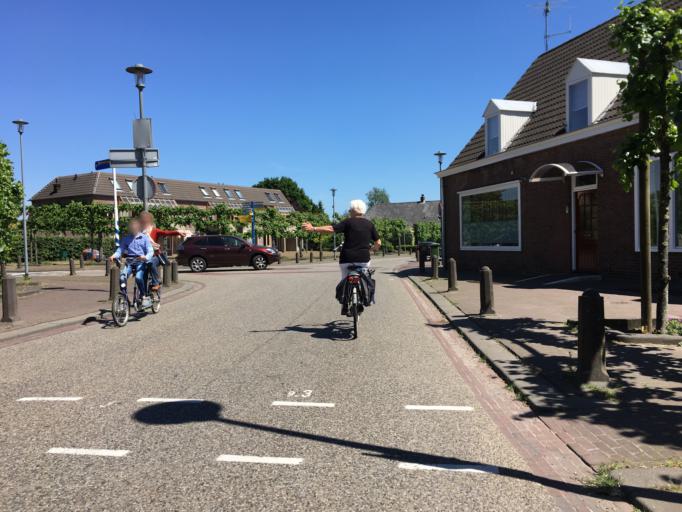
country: NL
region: Gelderland
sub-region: Gemeente Maasdriel
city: Hedel
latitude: 51.7486
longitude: 5.2250
